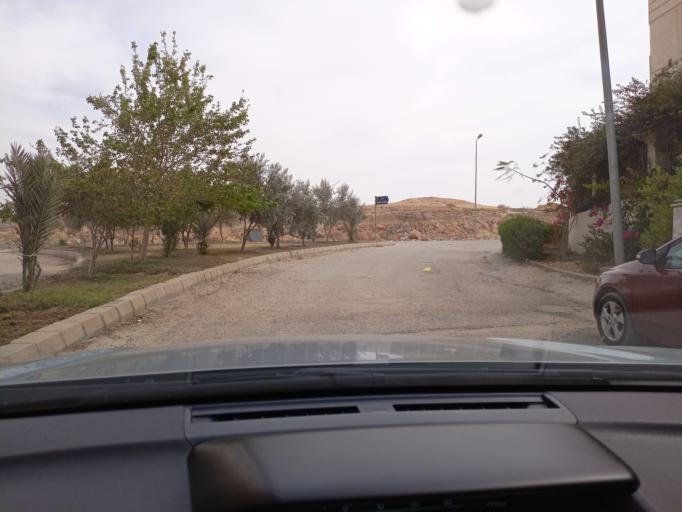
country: EG
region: Muhafazat al Qalyubiyah
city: Al Khankah
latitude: 30.2437
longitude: 31.4944
